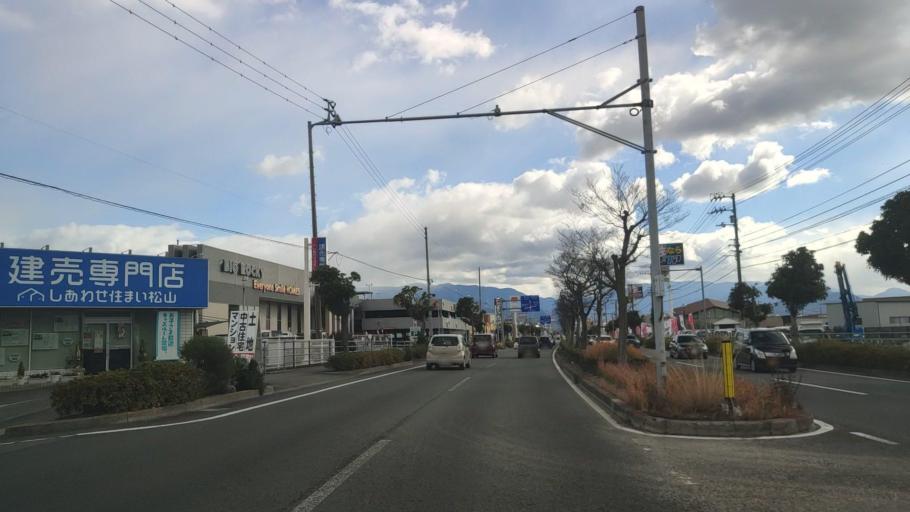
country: JP
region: Ehime
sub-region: Shikoku-chuo Shi
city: Matsuyama
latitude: 33.8175
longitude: 132.7936
